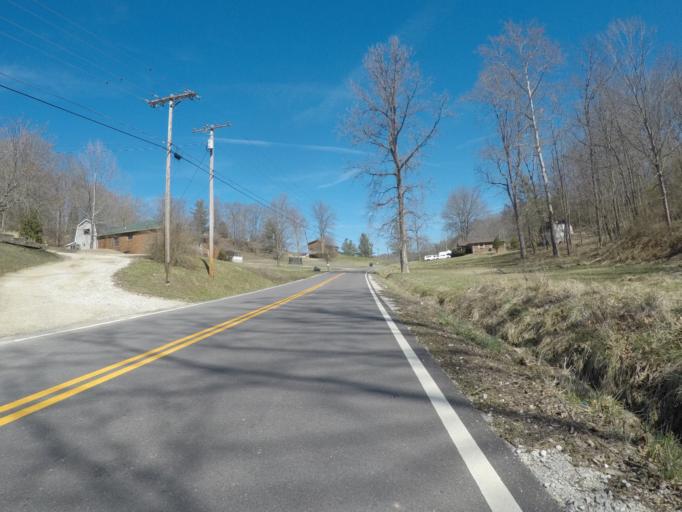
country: US
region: Ohio
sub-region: Lawrence County
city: Burlington
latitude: 38.4537
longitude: -82.5393
